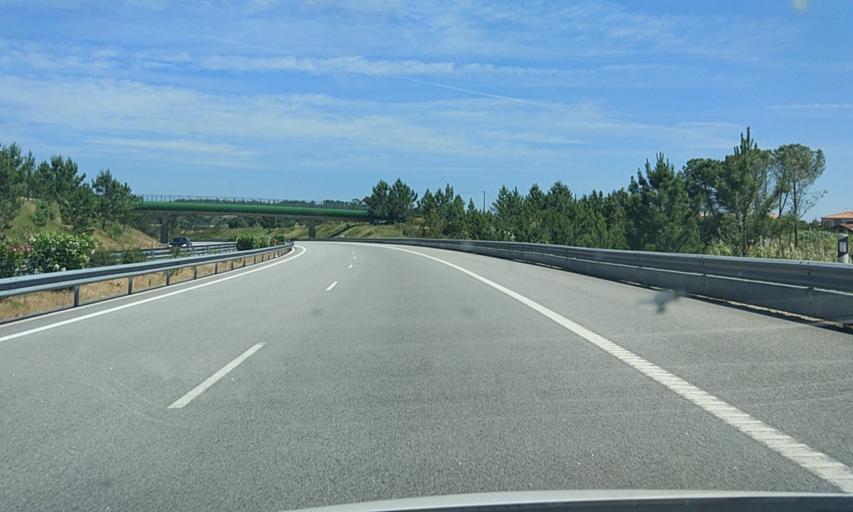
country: PT
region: Aveiro
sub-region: Mealhada
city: Pampilhosa do Botao
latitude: 40.2729
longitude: -8.5029
